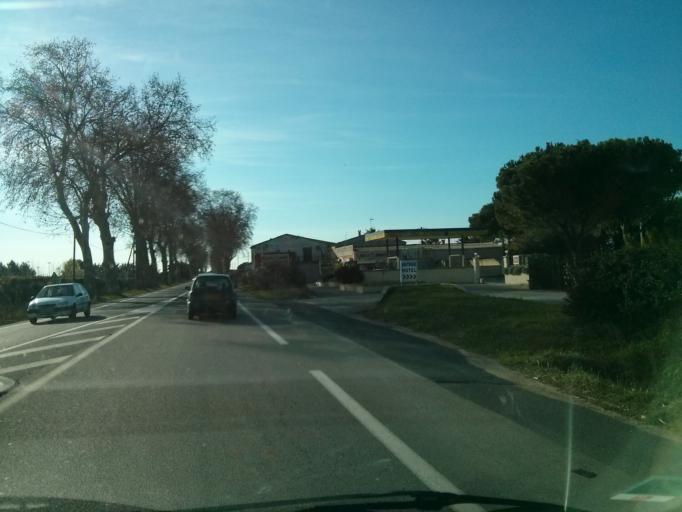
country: FR
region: Languedoc-Roussillon
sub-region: Departement du Gard
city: Gallargues-le-Montueux
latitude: 43.6917
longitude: 4.1622
